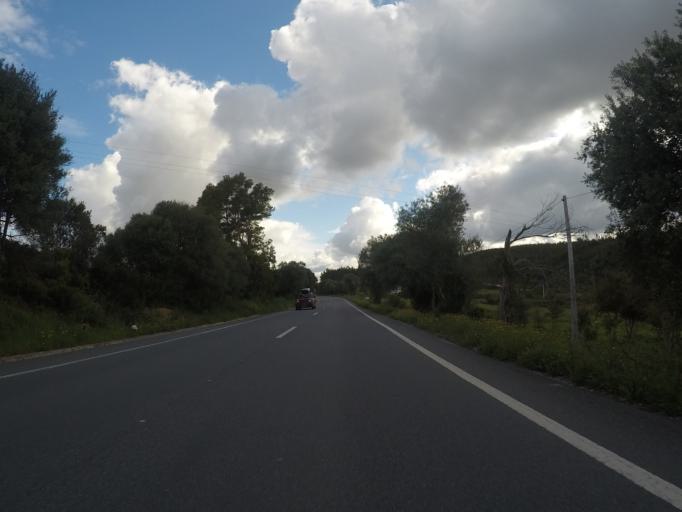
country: PT
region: Faro
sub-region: Aljezur
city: Aljezur
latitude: 37.2636
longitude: -8.8102
